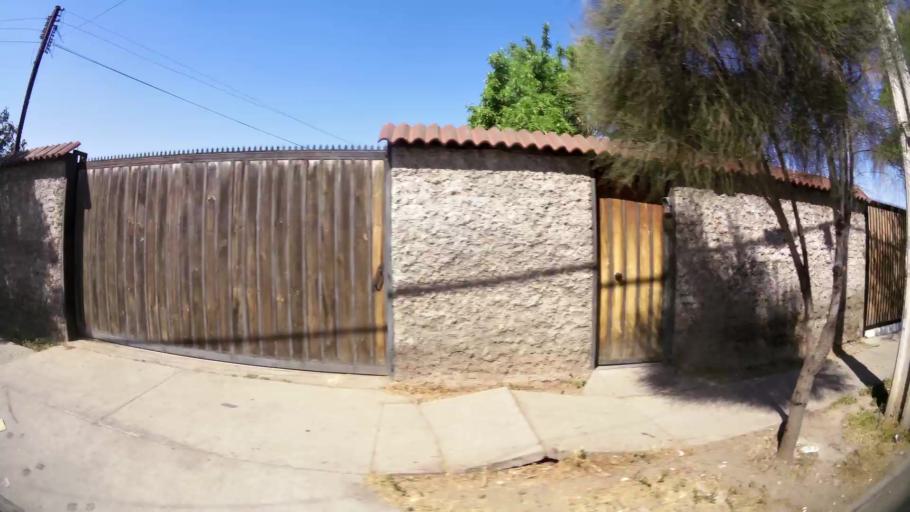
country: CL
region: Santiago Metropolitan
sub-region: Provincia de Santiago
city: Lo Prado
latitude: -33.5006
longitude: -70.7250
